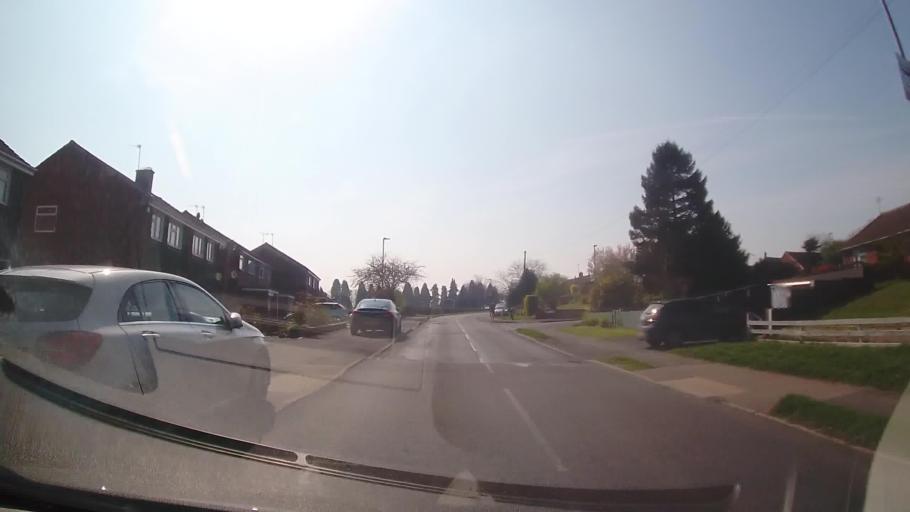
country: GB
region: England
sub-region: Leicestershire
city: Anstey
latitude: 52.6700
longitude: -1.1927
